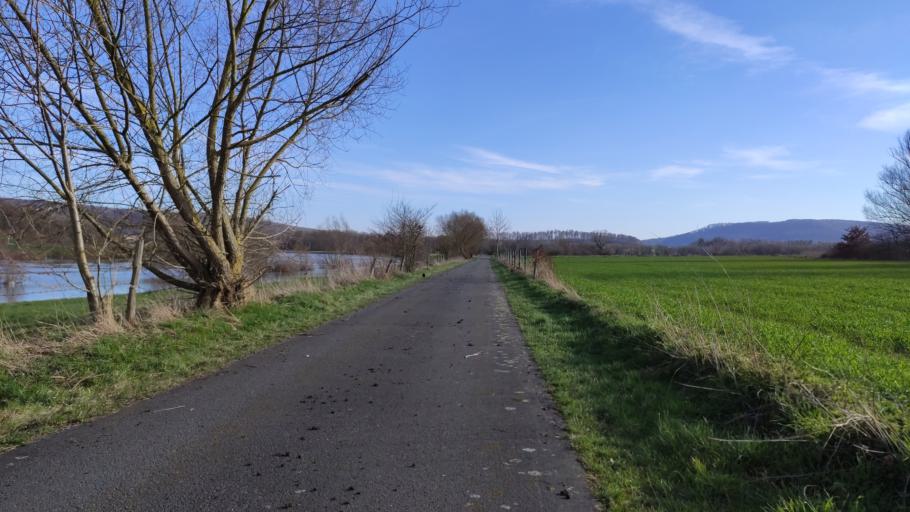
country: DE
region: Lower Saxony
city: Boffzen
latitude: 51.7429
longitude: 9.3741
